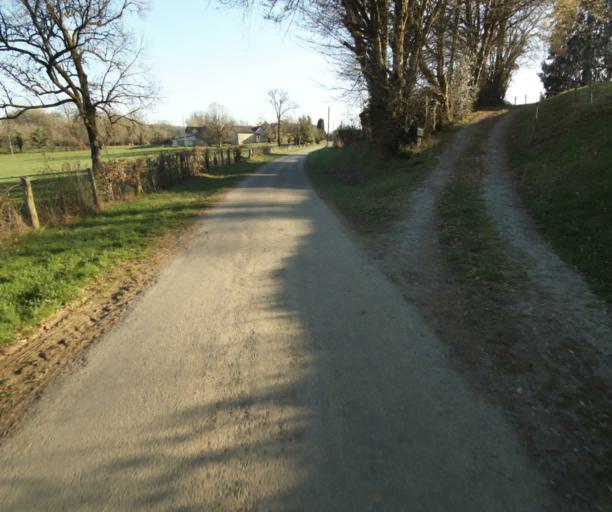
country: FR
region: Limousin
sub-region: Departement de la Correze
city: Saint-Clement
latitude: 45.3399
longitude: 1.6611
